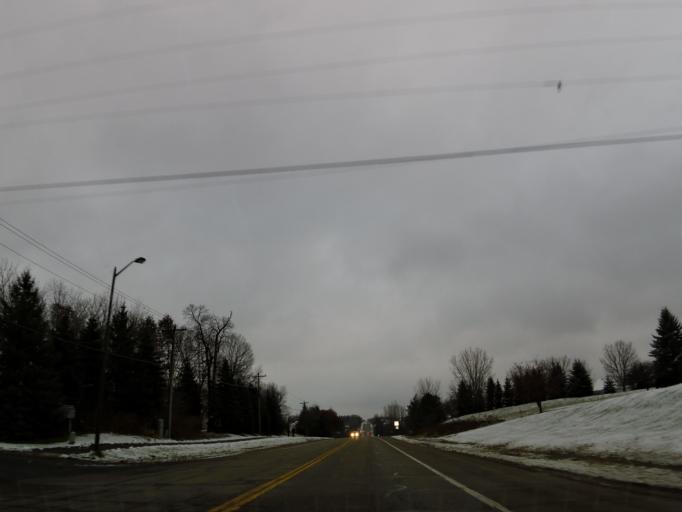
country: US
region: Minnesota
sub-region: Dakota County
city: Apple Valley
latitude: 44.7073
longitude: -93.2380
